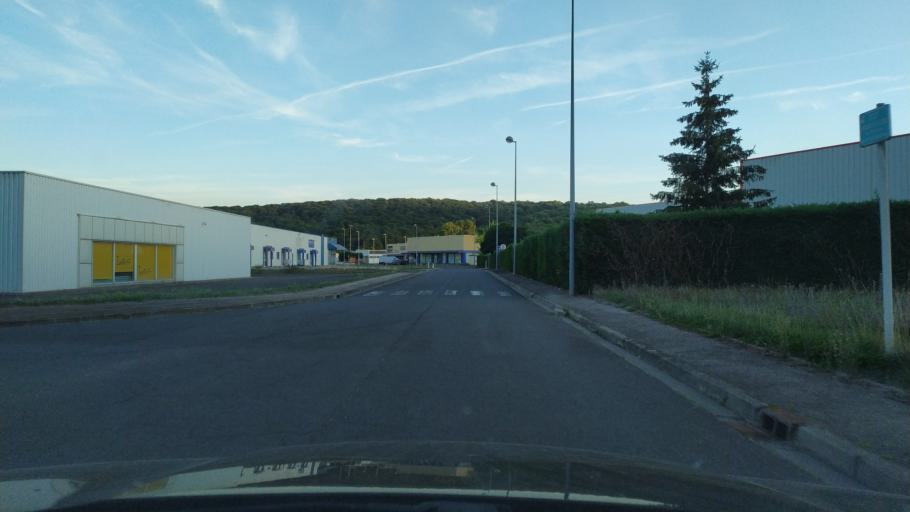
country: FR
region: Lorraine
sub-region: Departement de la Moselle
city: Jouy-aux-Arches
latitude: 49.0780
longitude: 6.0958
